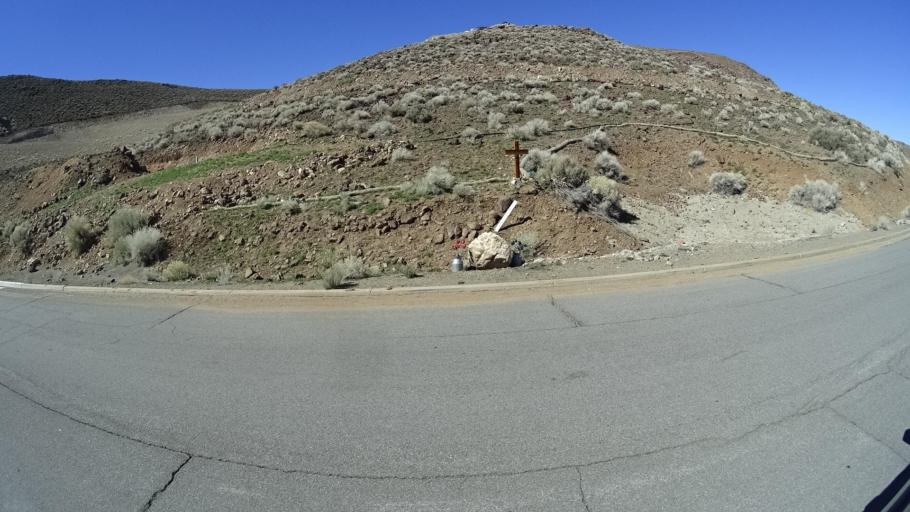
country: US
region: Nevada
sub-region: Washoe County
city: Sparks
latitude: 39.4789
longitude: -119.7268
